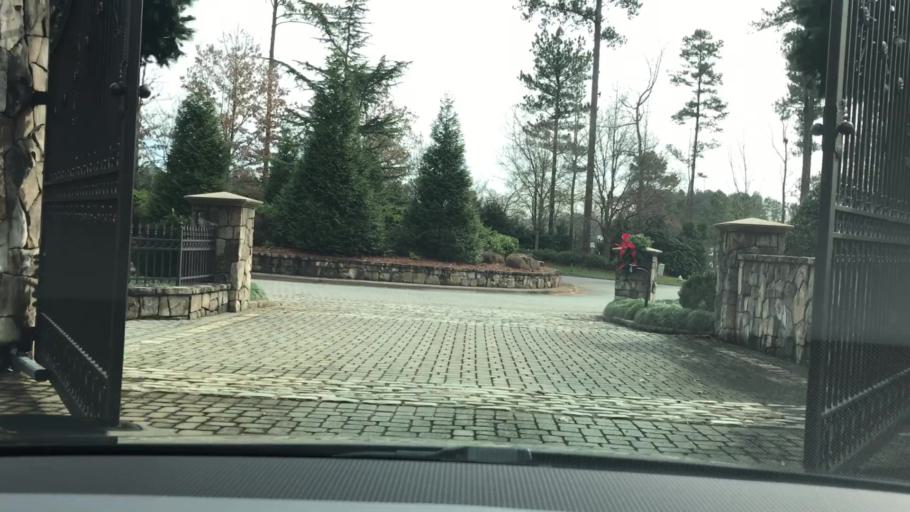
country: US
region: Georgia
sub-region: Gwinnett County
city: Suwanee
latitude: 34.0730
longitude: -84.1094
